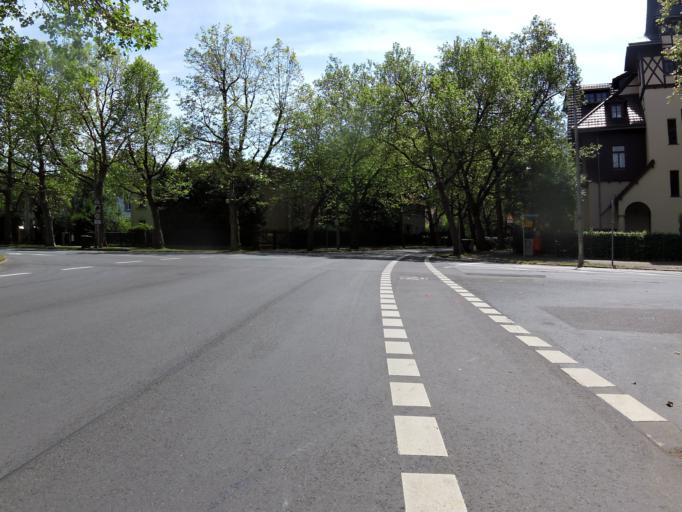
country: DE
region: Saxony
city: Leipzig
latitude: 51.3172
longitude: 12.4138
